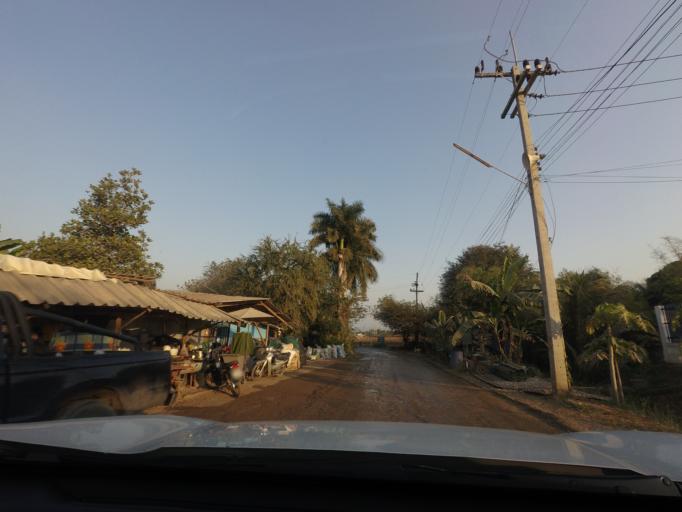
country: TH
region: Nakhon Ratchasima
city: Pak Chong
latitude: 14.6433
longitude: 101.4043
